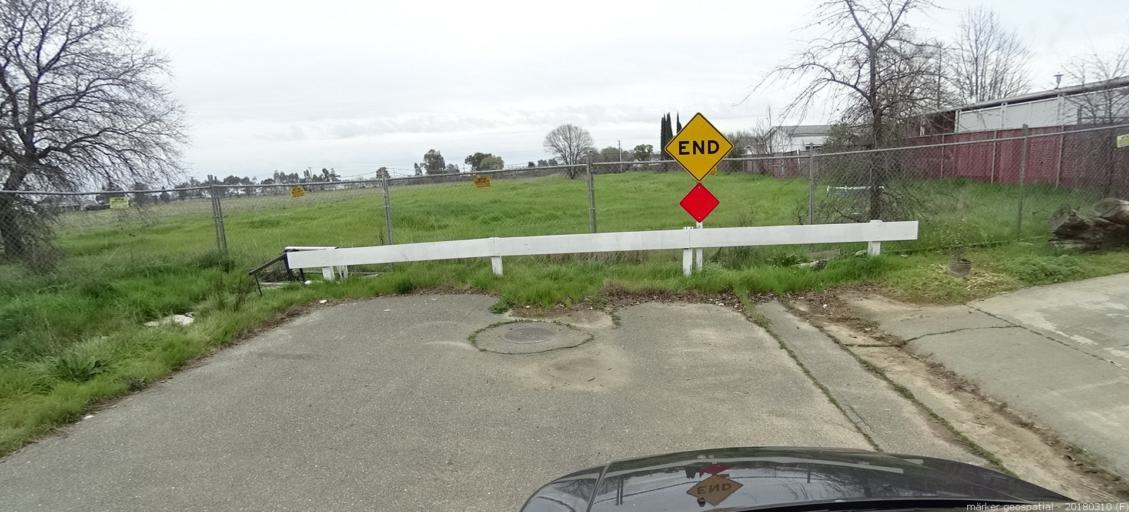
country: US
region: California
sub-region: Sacramento County
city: Florin
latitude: 38.4853
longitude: -121.3836
